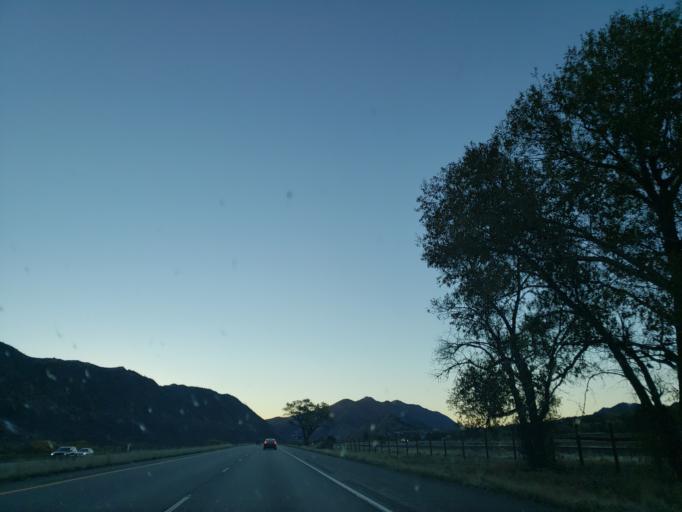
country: US
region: Colorado
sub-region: Garfield County
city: New Castle
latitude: 39.5659
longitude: -107.4943
